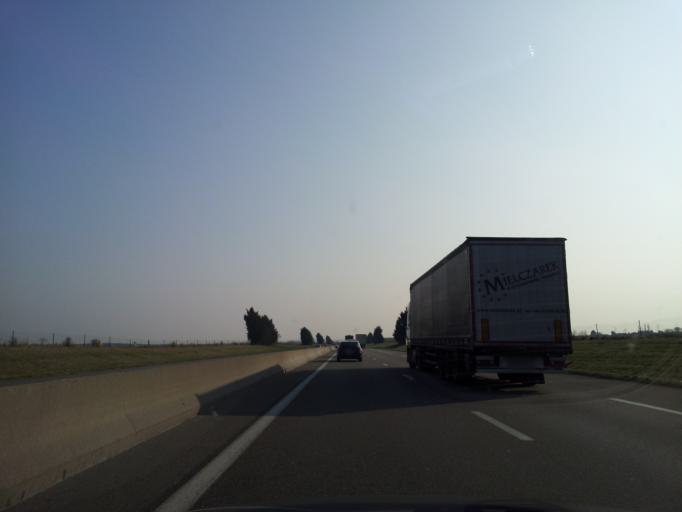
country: FR
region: Alsace
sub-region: Departement du Haut-Rhin
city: Battenheim
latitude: 47.8245
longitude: 7.3937
